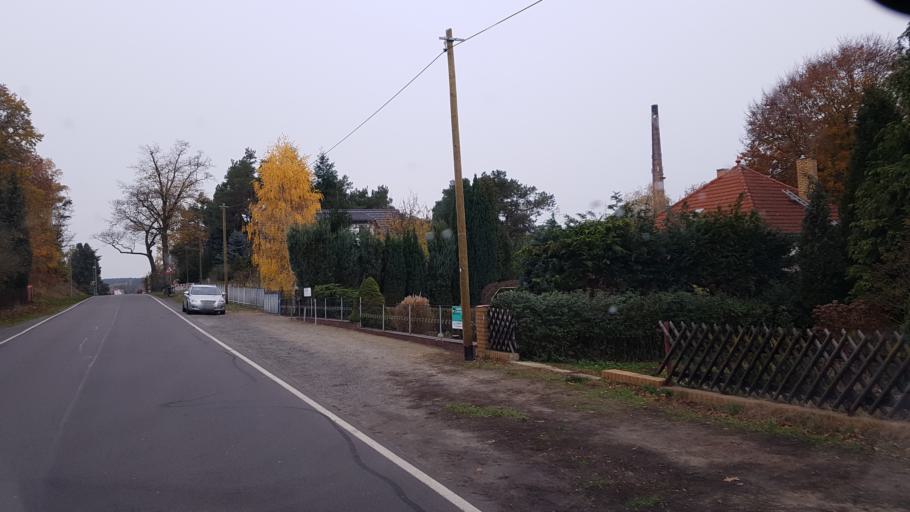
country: DE
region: Brandenburg
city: Crinitz
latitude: 51.7428
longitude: 13.7768
